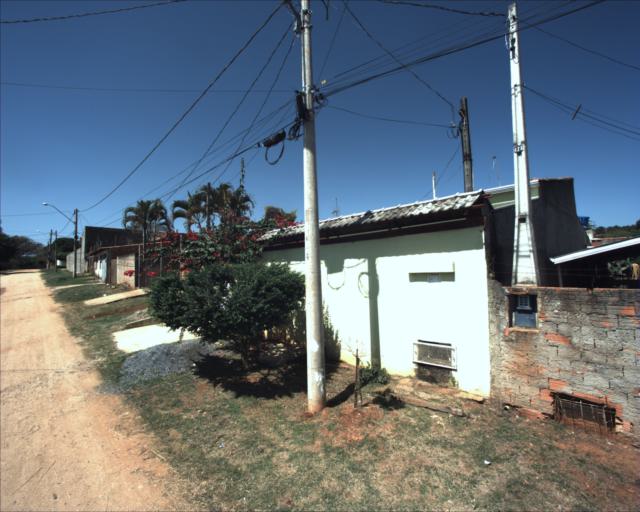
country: BR
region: Sao Paulo
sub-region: Aracoiaba Da Serra
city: Aracoiaba da Serra
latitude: -23.4398
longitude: -47.5392
